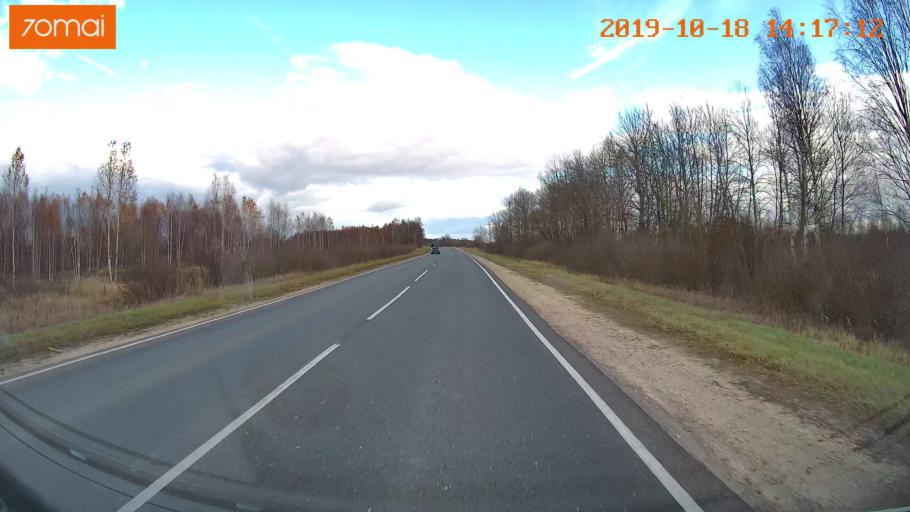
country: RU
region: Rjazan
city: Spas-Klepiki
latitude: 55.1400
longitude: 40.3641
